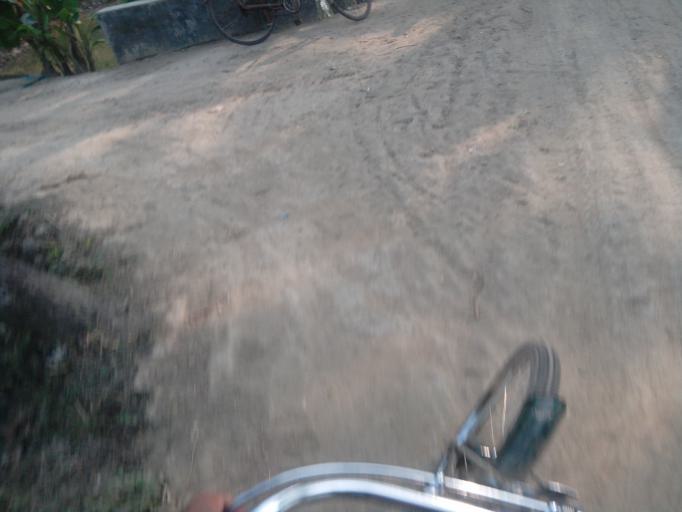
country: BD
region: Khulna
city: Kesabpur
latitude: 22.7674
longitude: 89.2287
